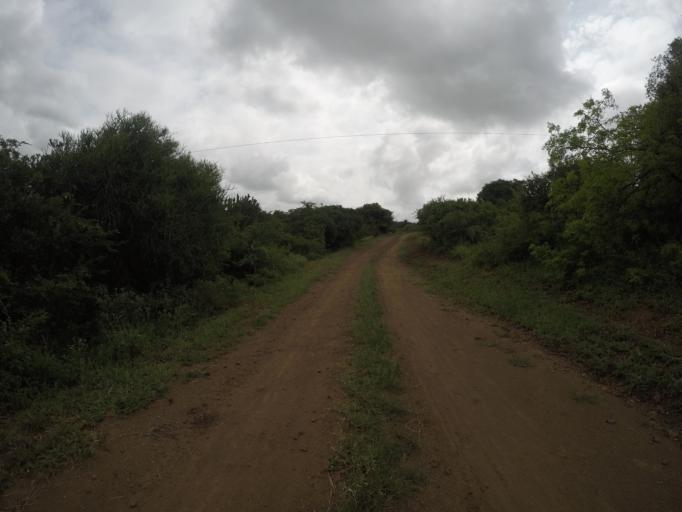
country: ZA
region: KwaZulu-Natal
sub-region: uThungulu District Municipality
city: Empangeni
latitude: -28.5877
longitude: 31.8701
